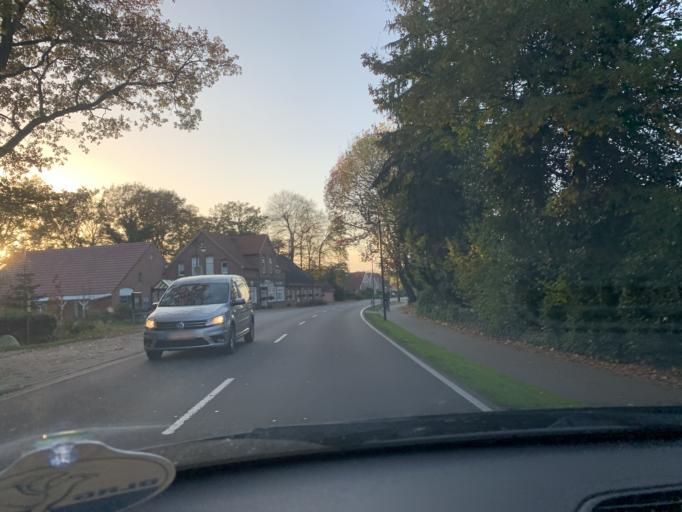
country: DE
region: Lower Saxony
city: Edewecht
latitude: 53.1216
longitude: 8.0206
